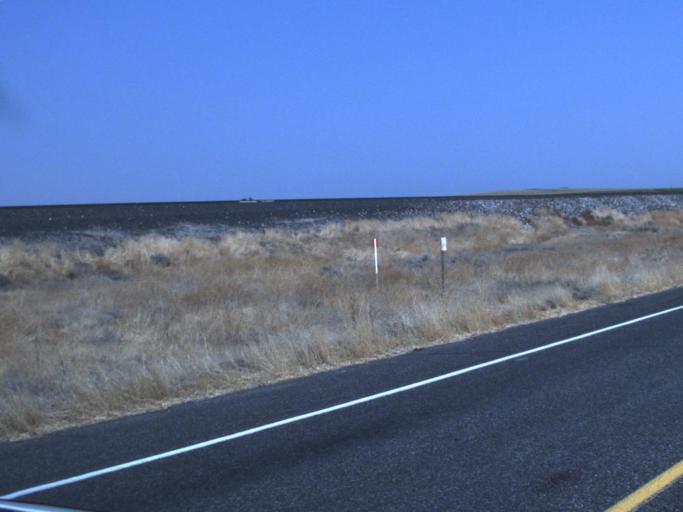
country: US
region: Washington
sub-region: Yakima County
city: Mabton
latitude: 46.2254
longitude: -120.0561
